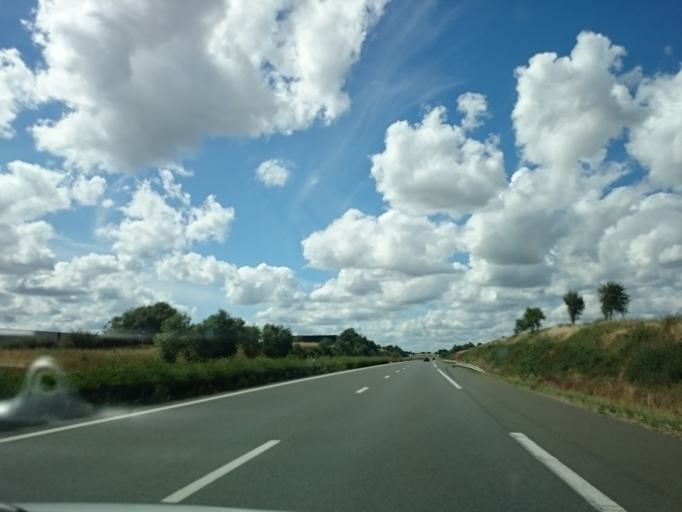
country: FR
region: Pays de la Loire
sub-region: Departement de Maine-et-Loire
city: Saint-Germain-des-Pres
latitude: 47.4353
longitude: -0.8218
